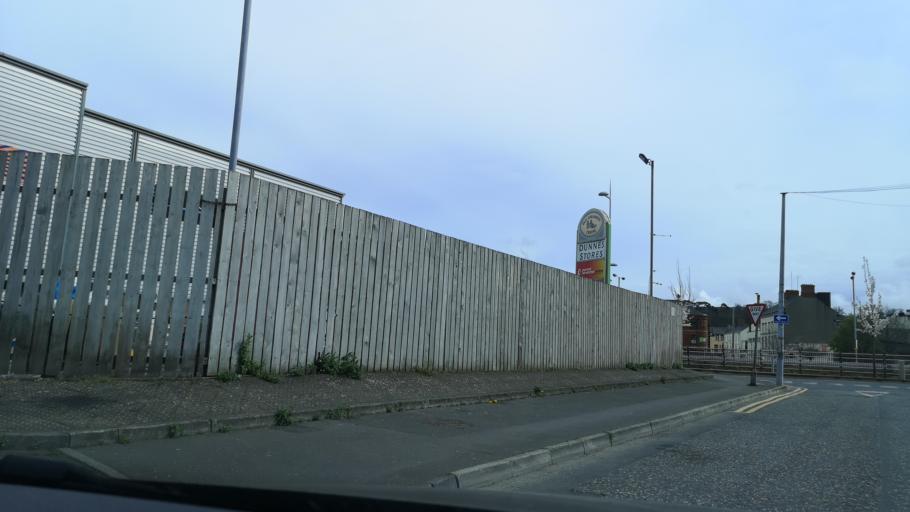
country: GB
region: Northern Ireland
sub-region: Newry and Mourne District
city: Newry
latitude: 54.1745
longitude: -6.3416
